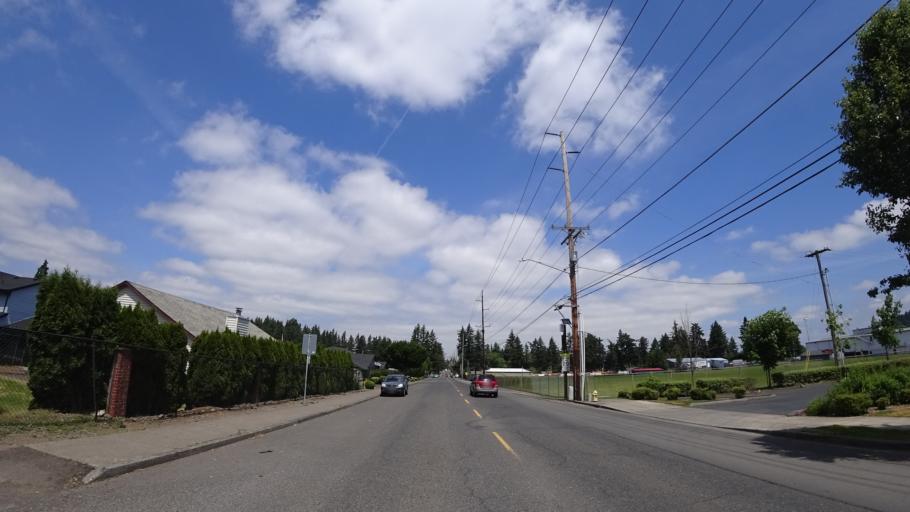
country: US
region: Oregon
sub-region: Multnomah County
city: Gresham
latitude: 45.4951
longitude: -122.4847
